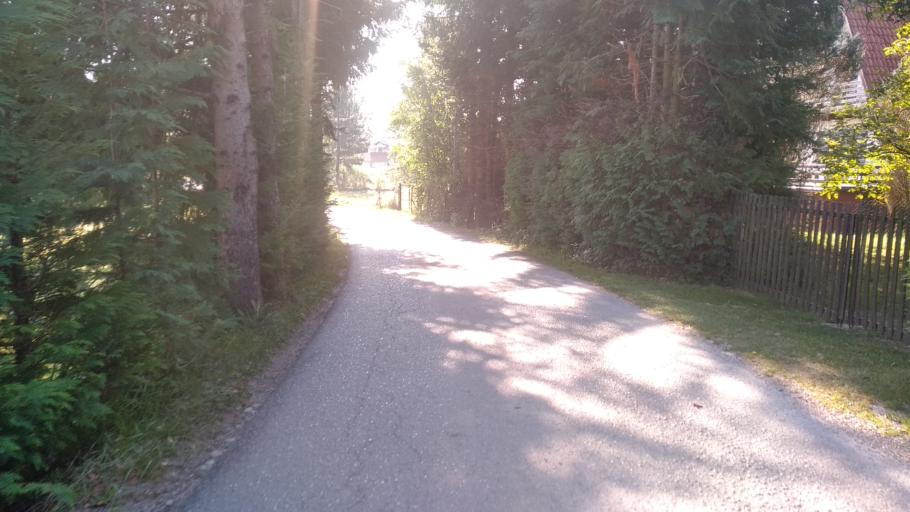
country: RS
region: Central Serbia
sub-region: Zlatiborski Okrug
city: Cajetina
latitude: 43.7355
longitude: 19.7192
